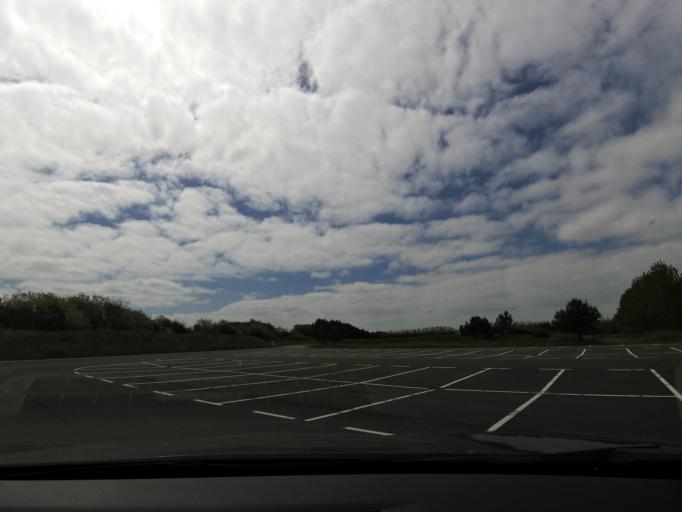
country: NL
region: South Holland
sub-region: Gemeente Goeree-Overflakkee
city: Ouddorp
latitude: 51.8234
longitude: 3.9115
